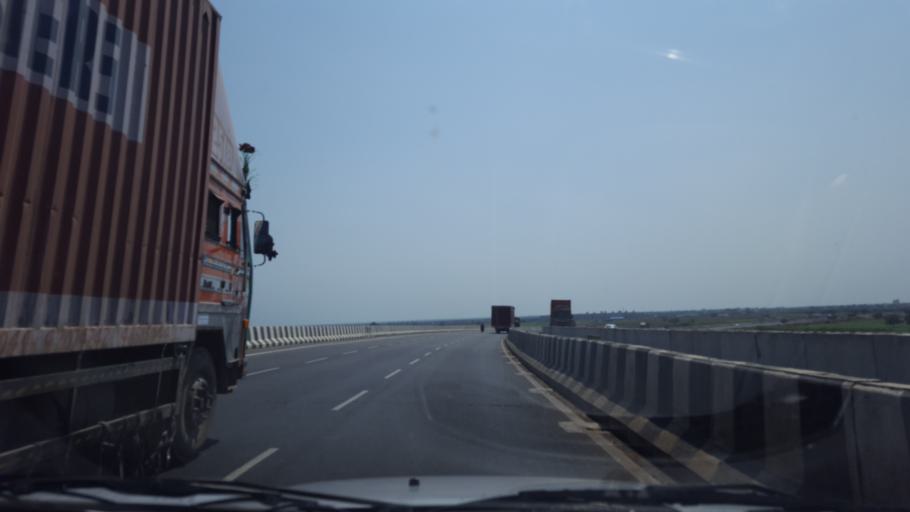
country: IN
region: Andhra Pradesh
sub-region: Prakasam
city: Ongole
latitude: 15.5153
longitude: 80.0712
